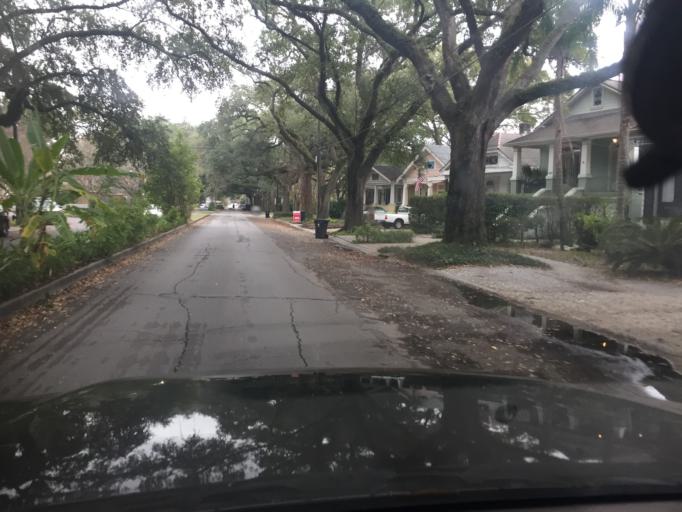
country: US
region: Louisiana
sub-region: Orleans Parish
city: New Orleans
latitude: 29.9760
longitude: -90.0833
